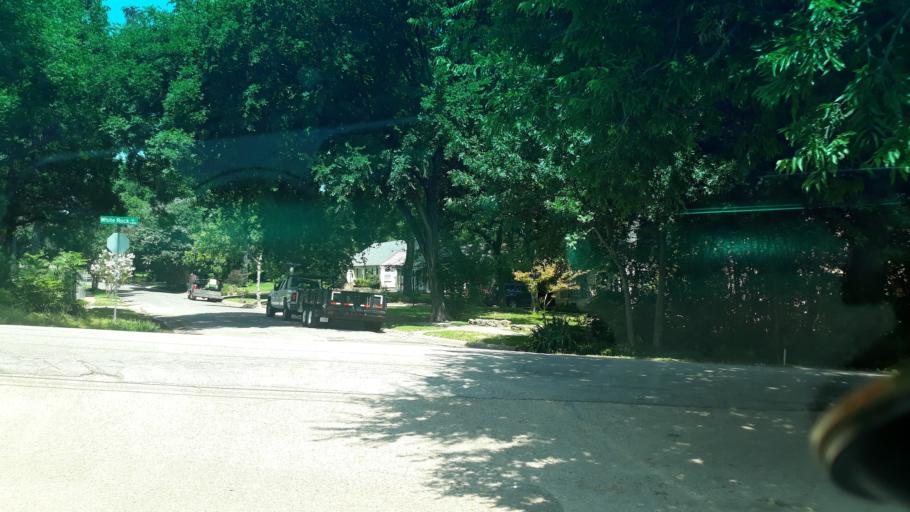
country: US
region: Texas
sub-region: Dallas County
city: Highland Park
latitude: 32.8167
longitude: -96.7355
